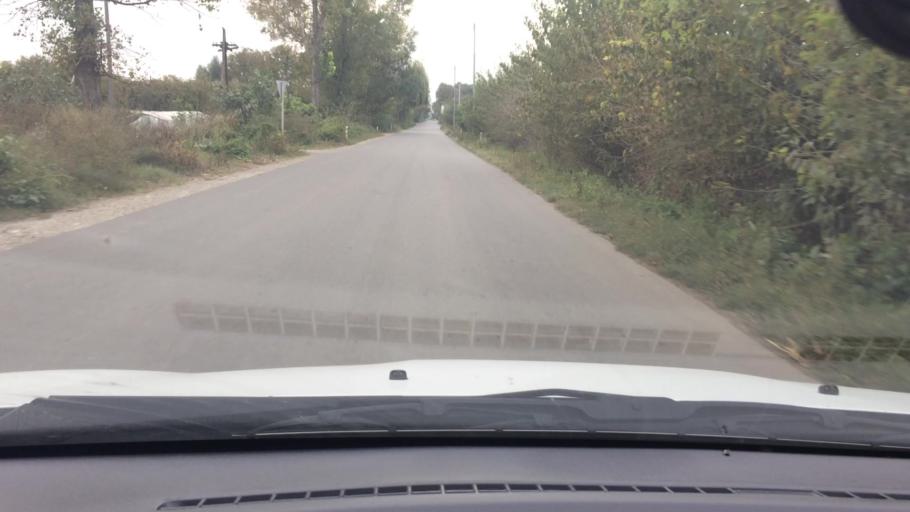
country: AM
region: Tavush
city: Bagratashen
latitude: 41.3333
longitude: 44.9125
